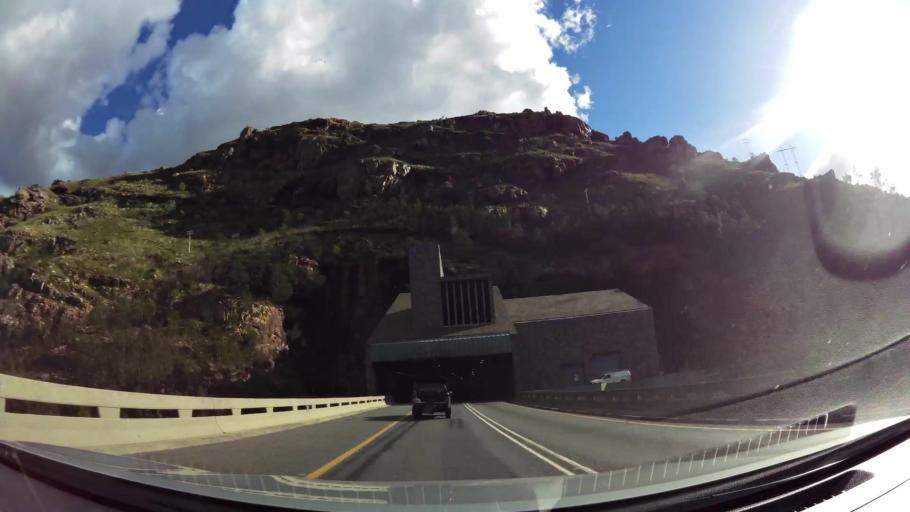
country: ZA
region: Western Cape
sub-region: Cape Winelands District Municipality
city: Paarl
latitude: -33.7331
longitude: 19.1141
